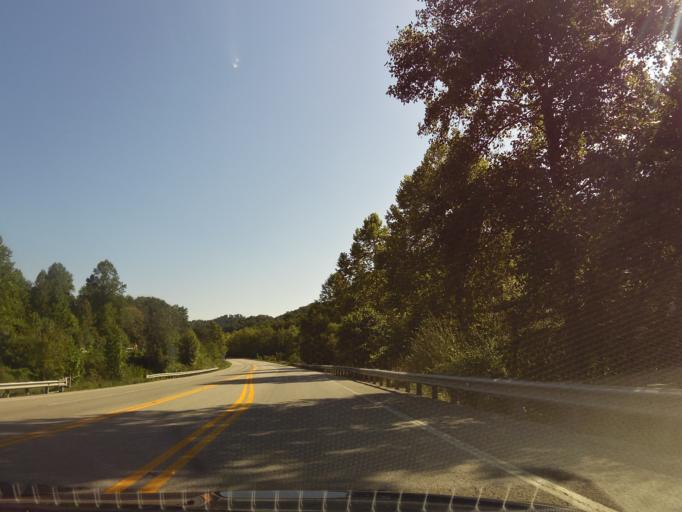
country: US
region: Kentucky
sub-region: Clay County
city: Manchester
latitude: 37.1283
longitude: -83.8705
